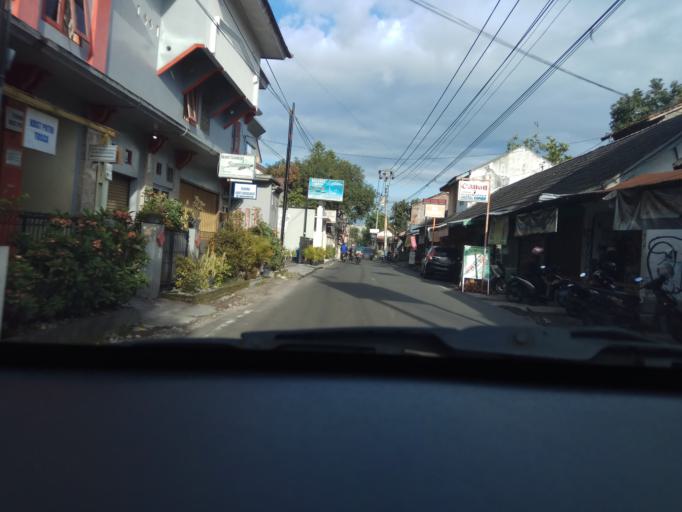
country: ID
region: Daerah Istimewa Yogyakarta
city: Depok
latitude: -7.7635
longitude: 110.4070
